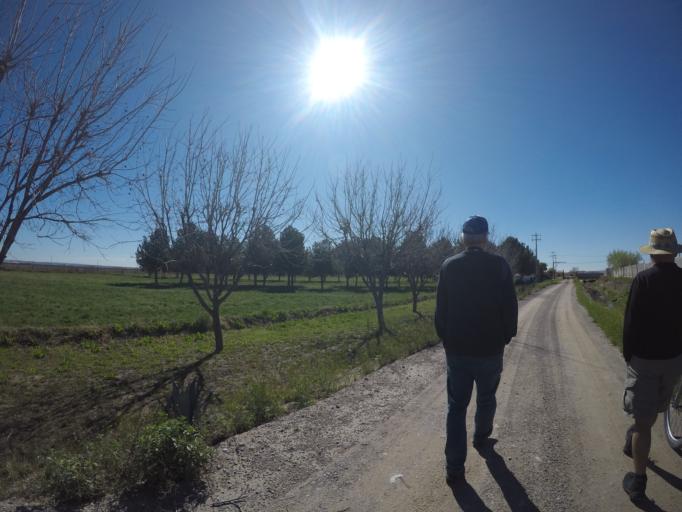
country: US
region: Texas
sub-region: El Paso County
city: Socorro
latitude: 31.6441
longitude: -106.3364
